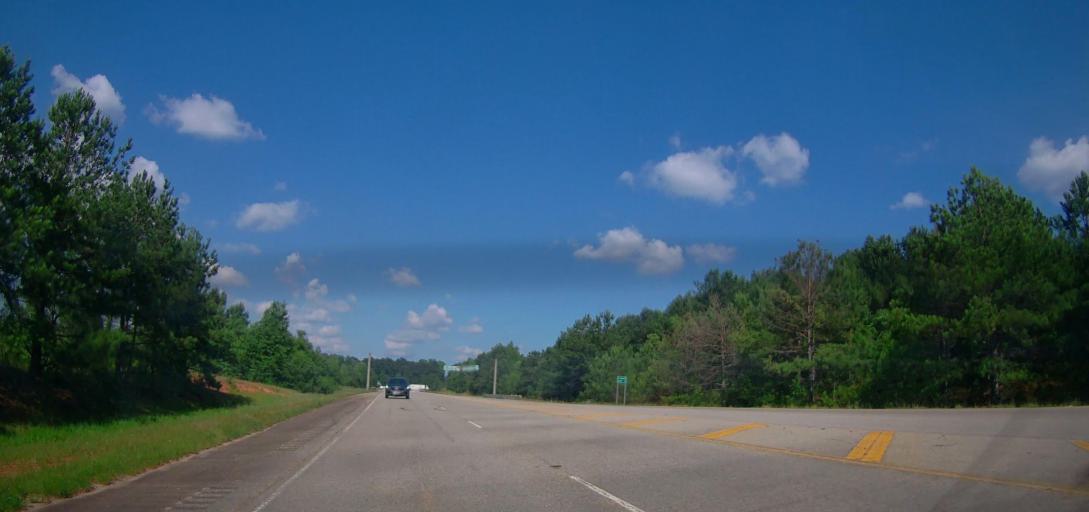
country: US
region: Georgia
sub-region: Henry County
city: Hampton
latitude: 33.3697
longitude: -84.3022
